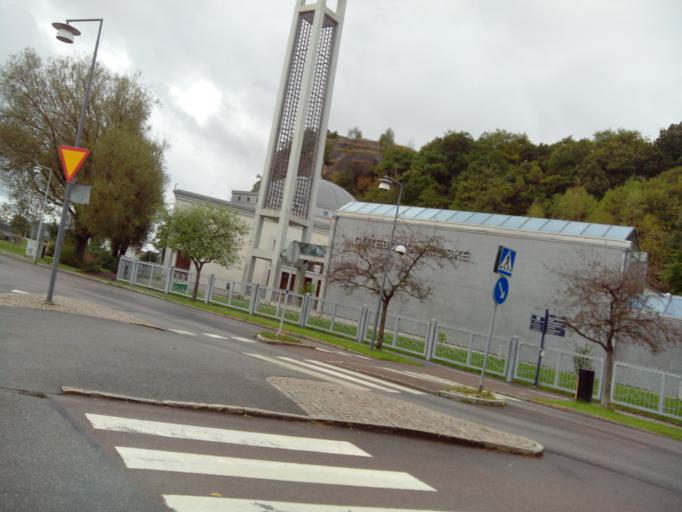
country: SE
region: Vaestra Goetaland
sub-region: Goteborg
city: Goeteborg
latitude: 57.7153
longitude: 11.9449
